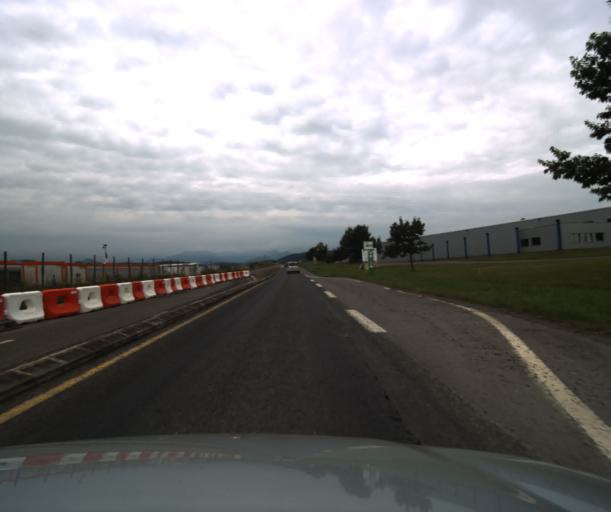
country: FR
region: Midi-Pyrenees
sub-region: Departement des Hautes-Pyrenees
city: Ossun
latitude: 43.1721
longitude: -0.0010
